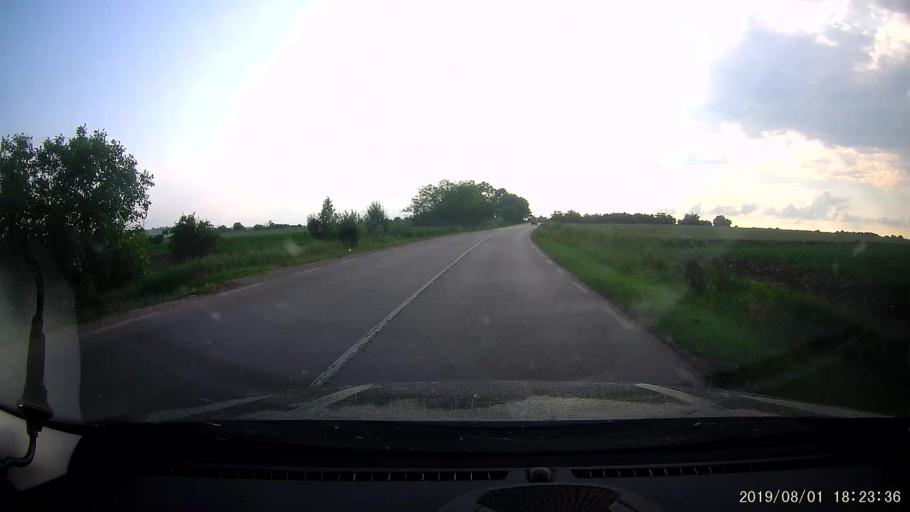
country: BG
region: Shumen
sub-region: Obshtina Kaolinovo
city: Kaolinovo
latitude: 43.6269
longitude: 27.0213
